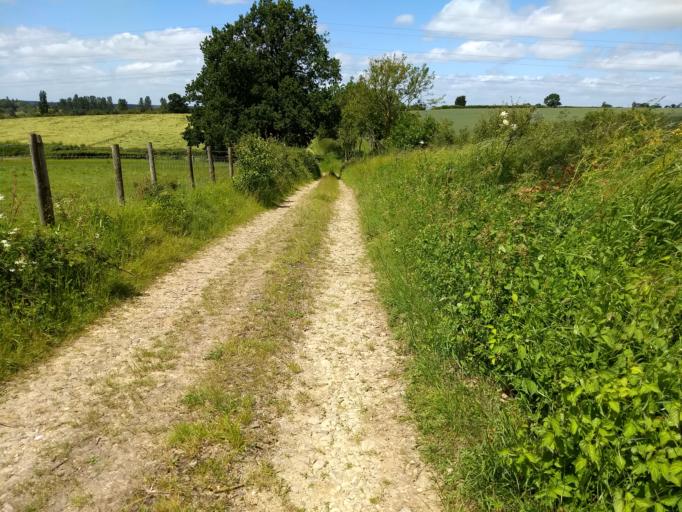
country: GB
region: England
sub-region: Milton Keynes
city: Calverton
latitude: 52.0220
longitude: -0.8635
